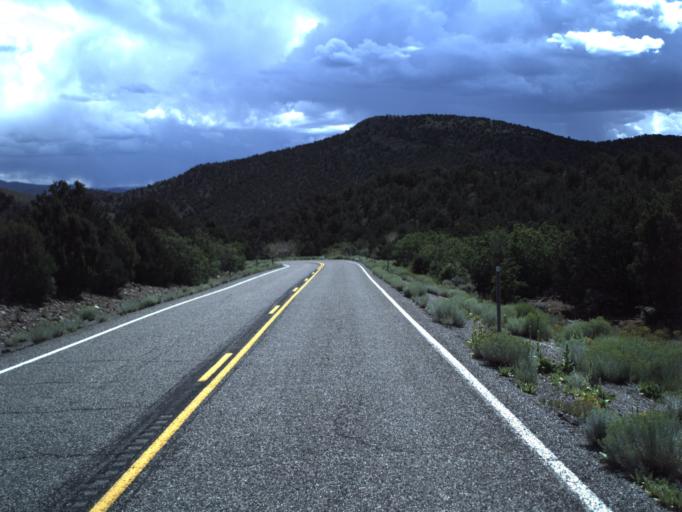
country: US
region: Utah
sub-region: Piute County
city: Junction
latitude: 38.2580
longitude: -112.2875
